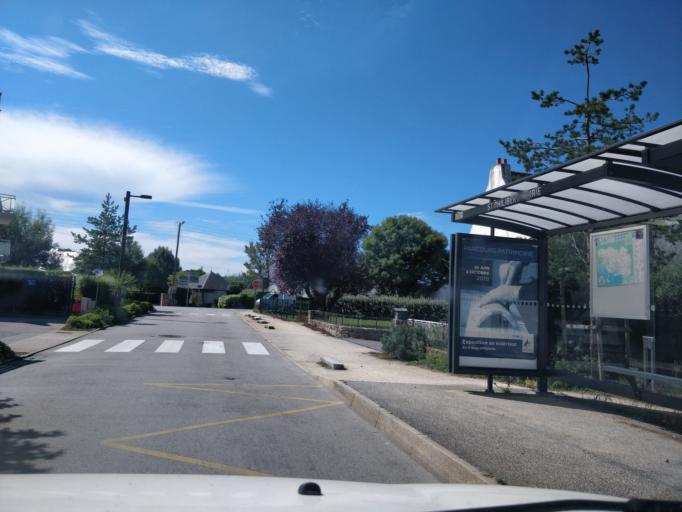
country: FR
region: Brittany
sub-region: Departement du Morbihan
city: Saint-Philibert
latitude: 47.5865
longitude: -3.0019
